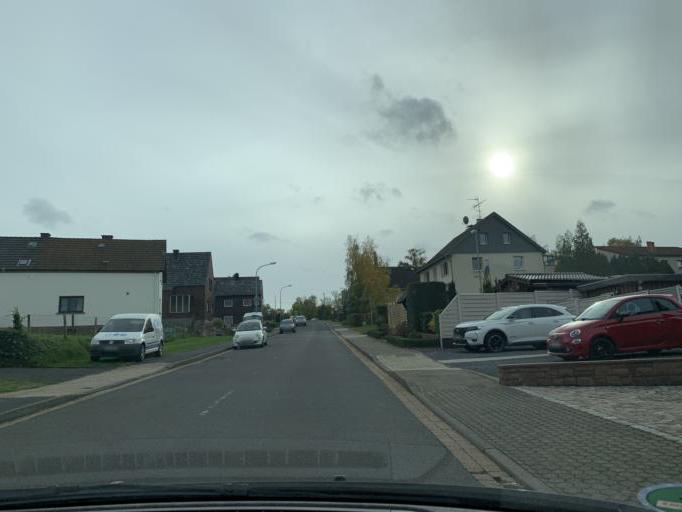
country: DE
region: North Rhine-Westphalia
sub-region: Regierungsbezirk Koln
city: Nideggen
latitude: 50.7119
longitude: 6.4942
